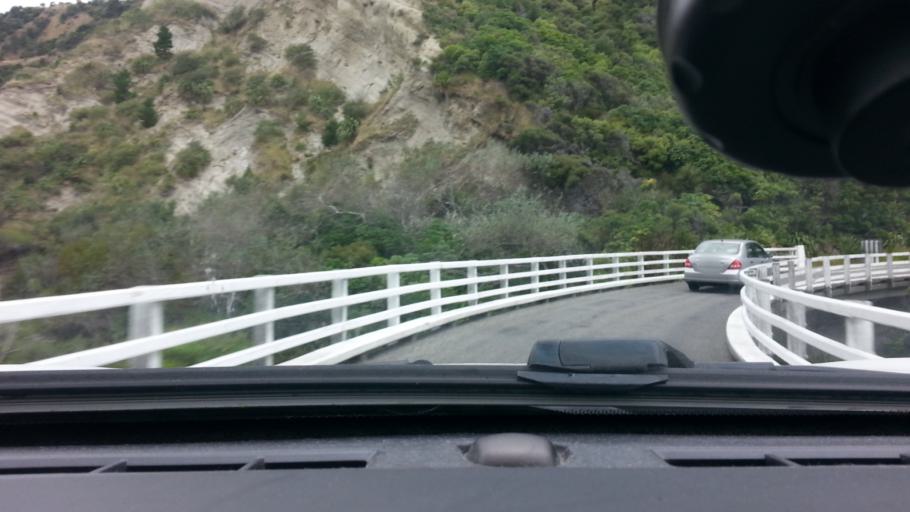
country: NZ
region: Wellington
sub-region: South Wairarapa District
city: Waipawa
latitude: -41.4403
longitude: 175.2203
